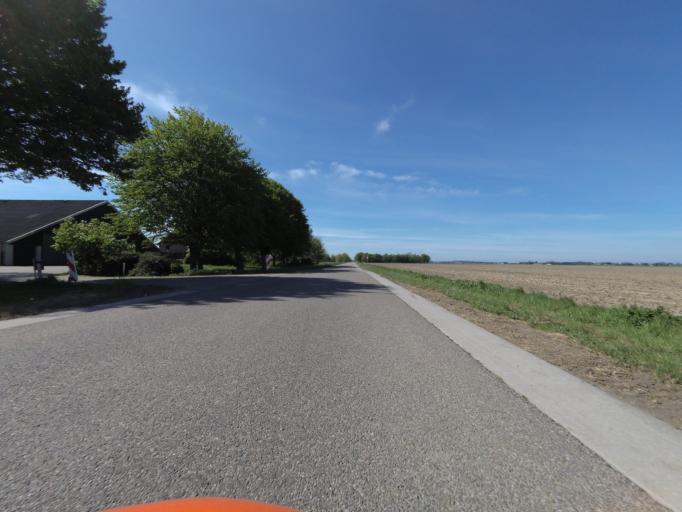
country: NL
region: Flevoland
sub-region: Gemeente Dronten
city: Biddinghuizen
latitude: 52.4292
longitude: 5.6916
